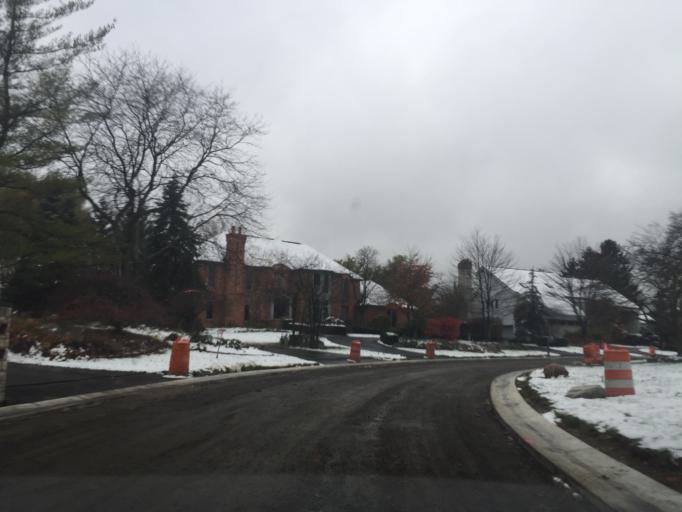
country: US
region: Michigan
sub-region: Oakland County
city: Bloomfield Hills
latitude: 42.6001
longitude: -83.2718
